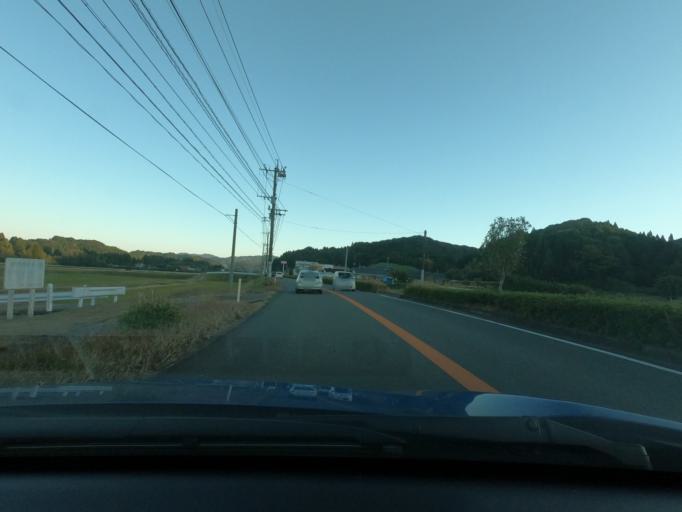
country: JP
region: Kagoshima
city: Satsumasendai
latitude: 31.8003
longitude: 130.4000
